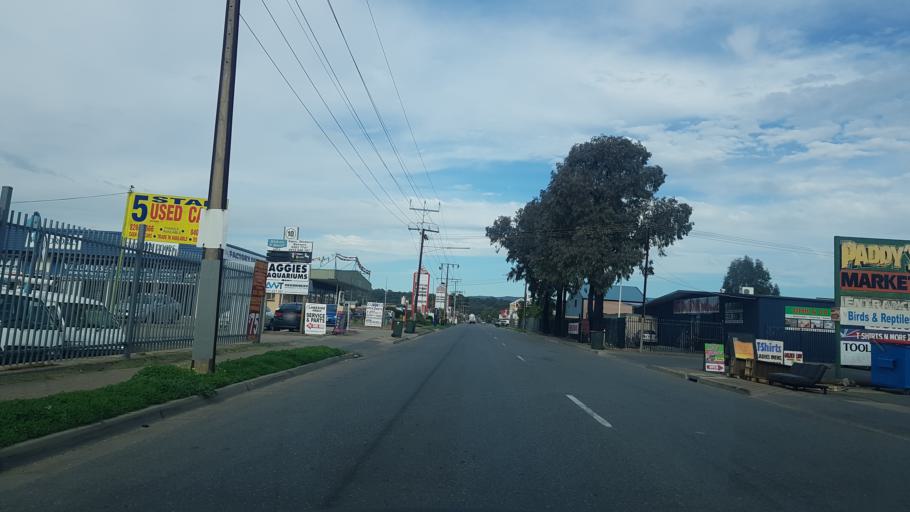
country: AU
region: South Australia
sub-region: Salisbury
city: Ingle Farm
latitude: -34.8129
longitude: 138.6295
